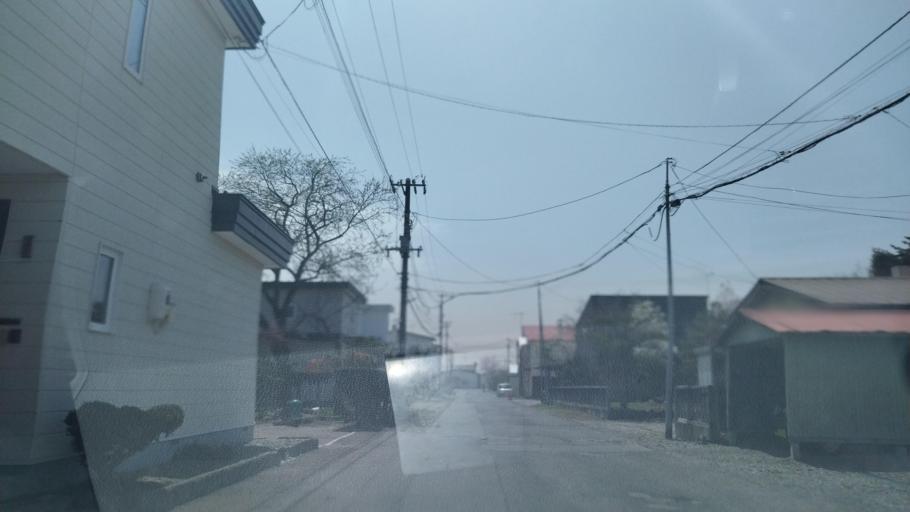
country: JP
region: Hokkaido
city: Obihiro
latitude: 42.9331
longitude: 143.1891
